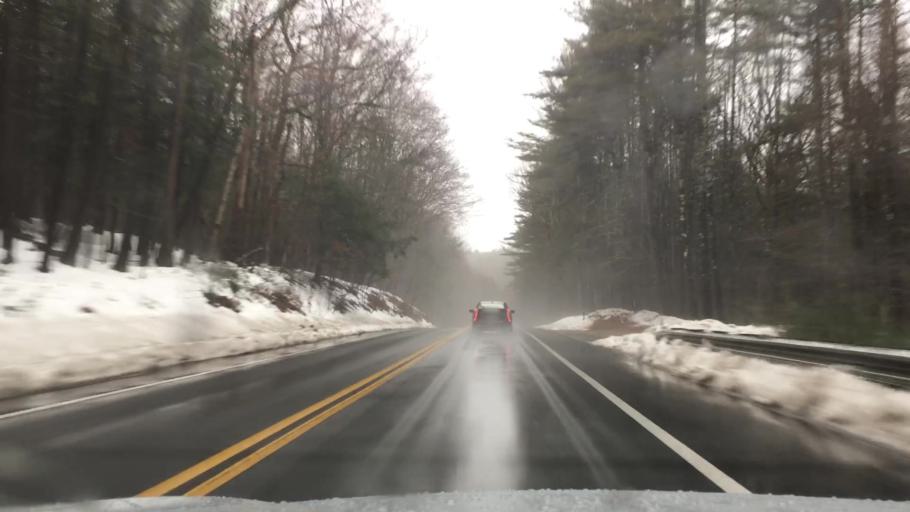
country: US
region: Massachusetts
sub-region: Franklin County
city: Shutesbury
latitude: 42.4259
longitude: -72.3977
